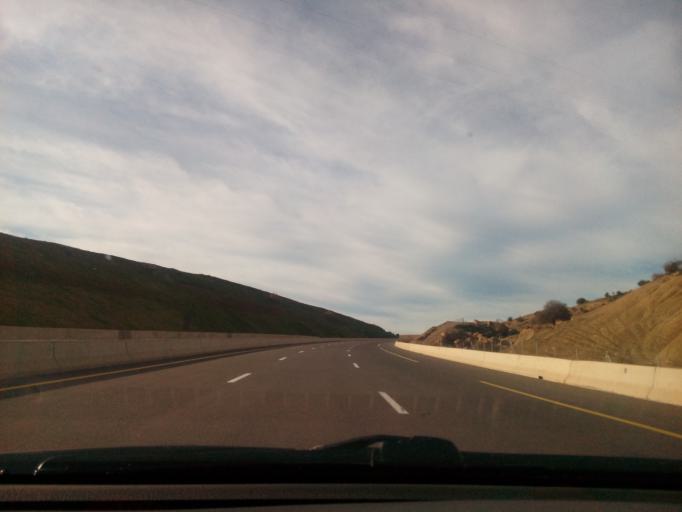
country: DZ
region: Tlemcen
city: Nedroma
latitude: 34.8984
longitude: -1.6543
